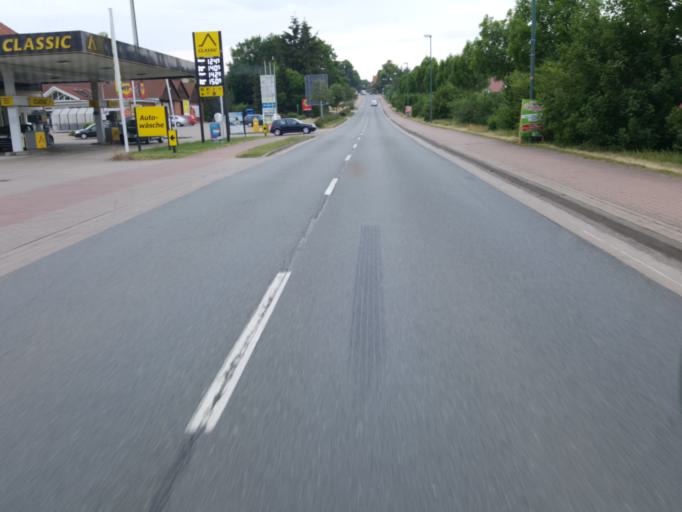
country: DE
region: Lower Saxony
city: Rehburg-Loccum
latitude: 52.4560
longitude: 9.1513
